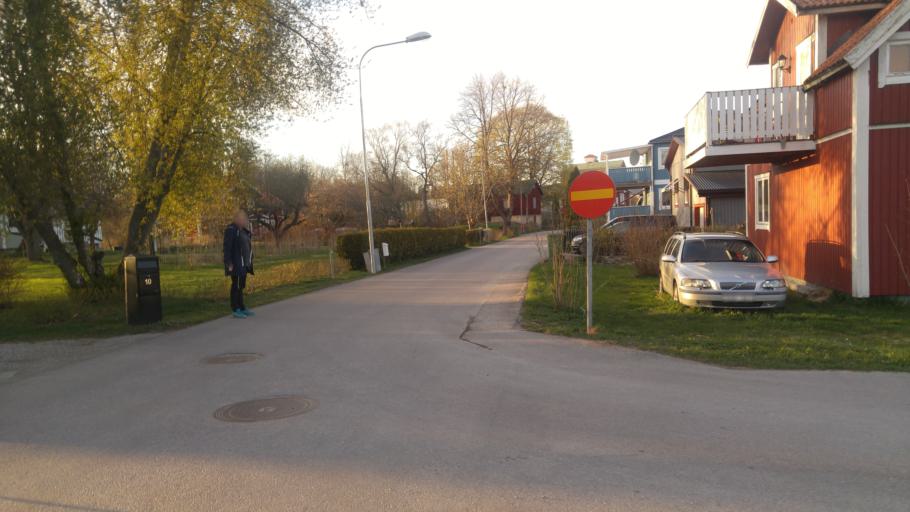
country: SE
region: Uppsala
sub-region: Heby Kommun
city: Morgongava
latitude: 59.9320
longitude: 16.9544
